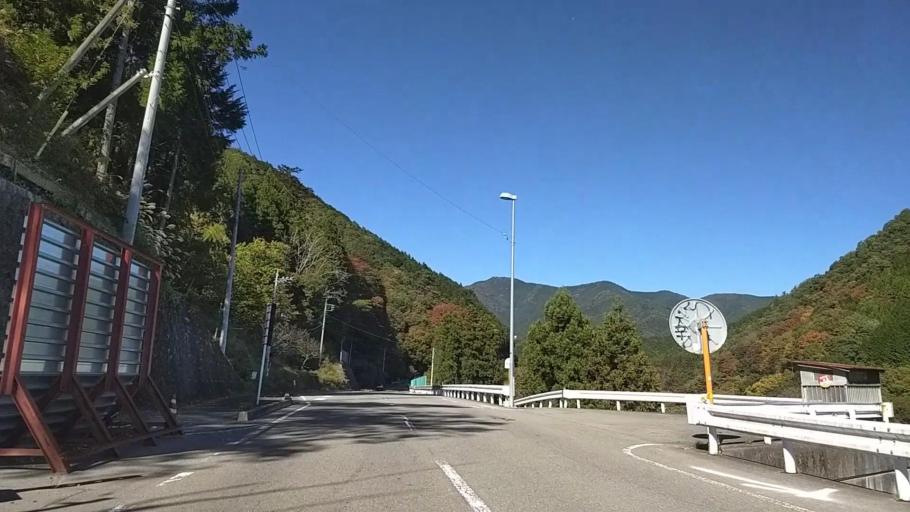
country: JP
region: Yamanashi
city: Uenohara
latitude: 35.6548
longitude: 139.0936
